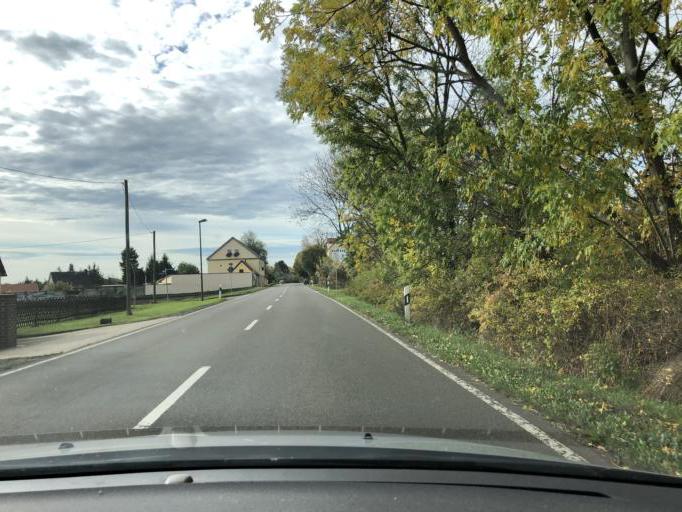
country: DE
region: Saxony
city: Elstertrebnitz
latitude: 51.1317
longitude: 12.2197
